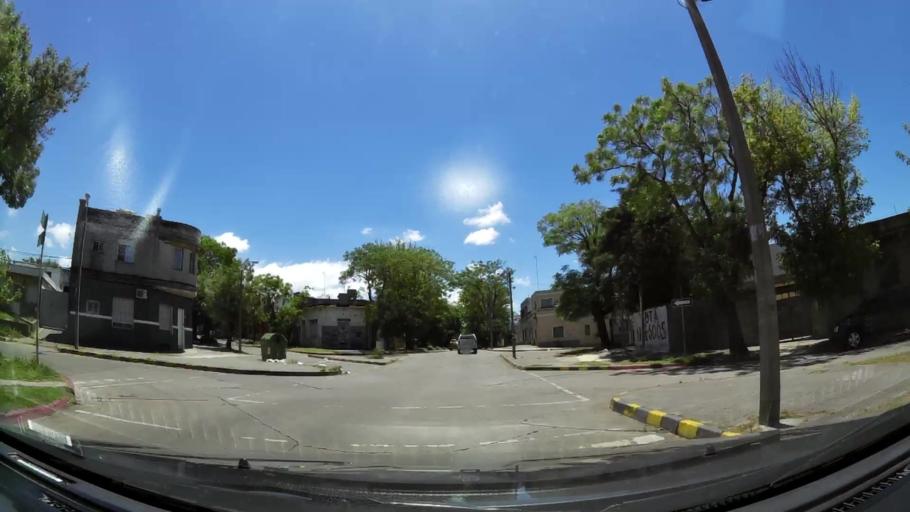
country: UY
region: Montevideo
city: Montevideo
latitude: -34.8984
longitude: -56.1365
